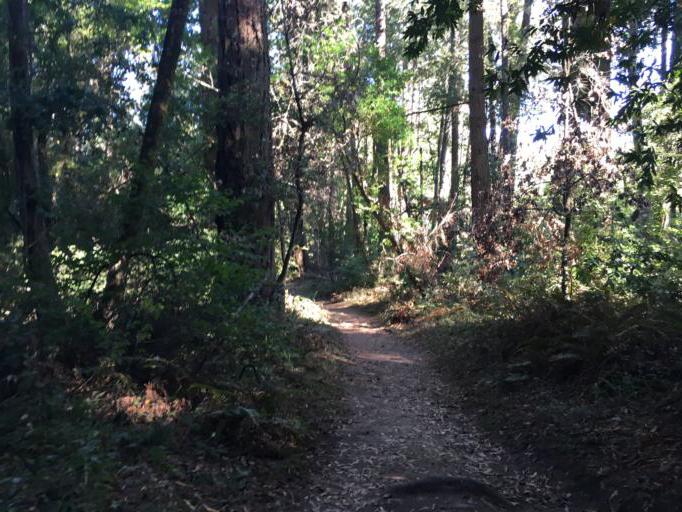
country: US
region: California
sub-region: Marin County
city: Inverness
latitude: 38.0363
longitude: -122.8043
